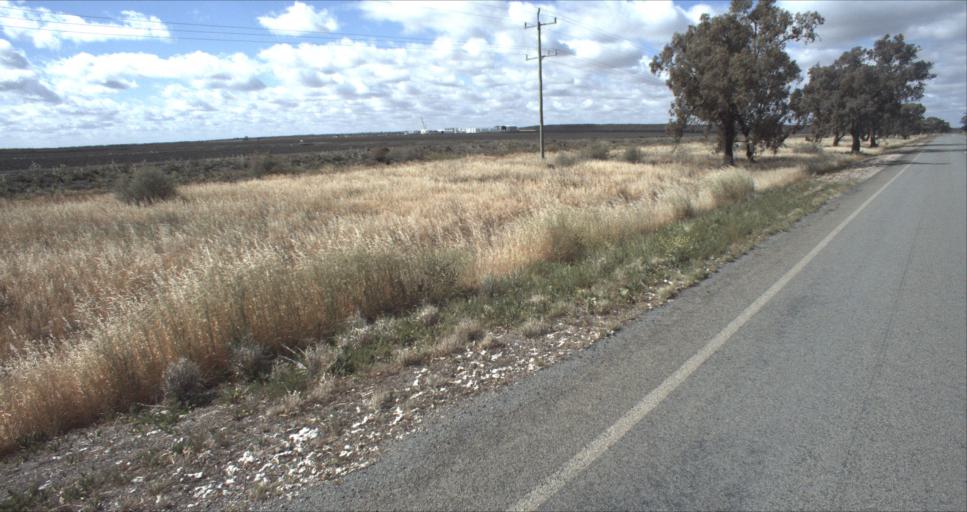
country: AU
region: New South Wales
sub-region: Murrumbidgee Shire
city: Darlington Point
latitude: -34.5638
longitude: 146.1685
